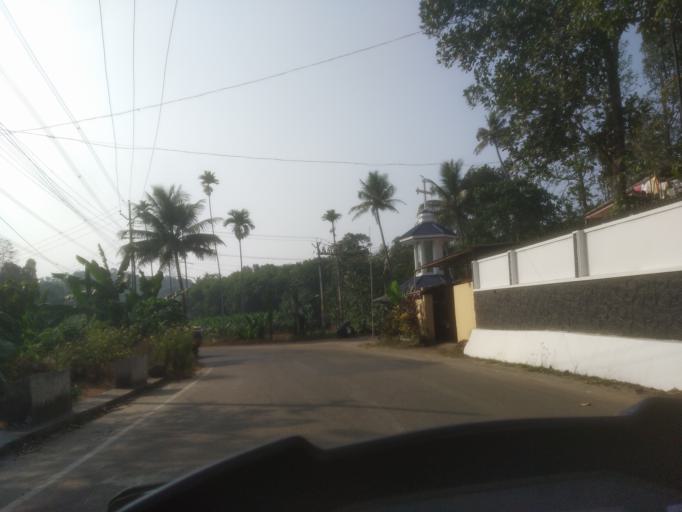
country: IN
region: Kerala
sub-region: Ernakulam
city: Piravam
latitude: 9.8343
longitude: 76.5181
